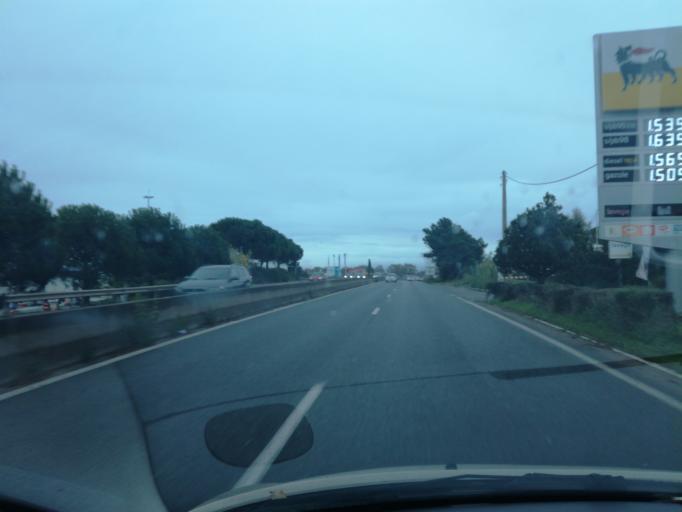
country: FR
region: Provence-Alpes-Cote d'Azur
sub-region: Departement du Var
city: Puget-sur-Argens
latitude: 43.4424
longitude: 6.7037
